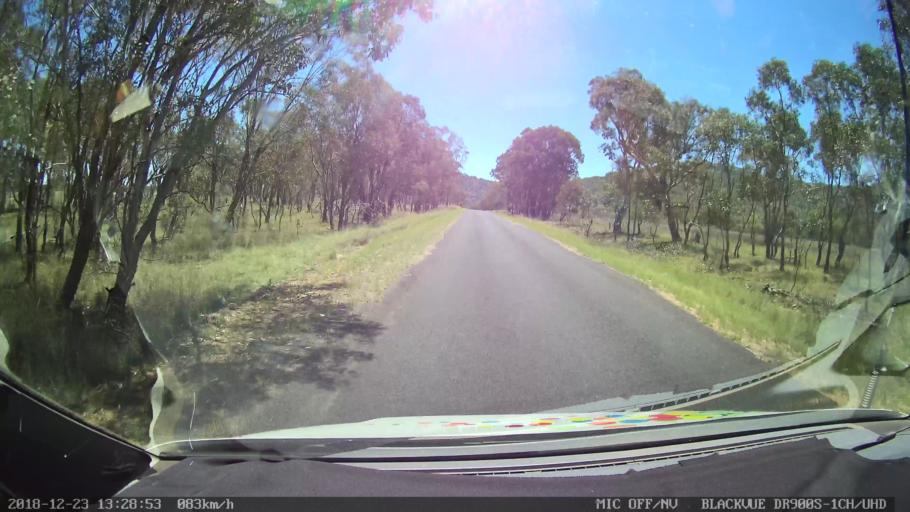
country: AU
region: New South Wales
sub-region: Armidale Dumaresq
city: Armidale
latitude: -30.4660
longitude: 151.3429
